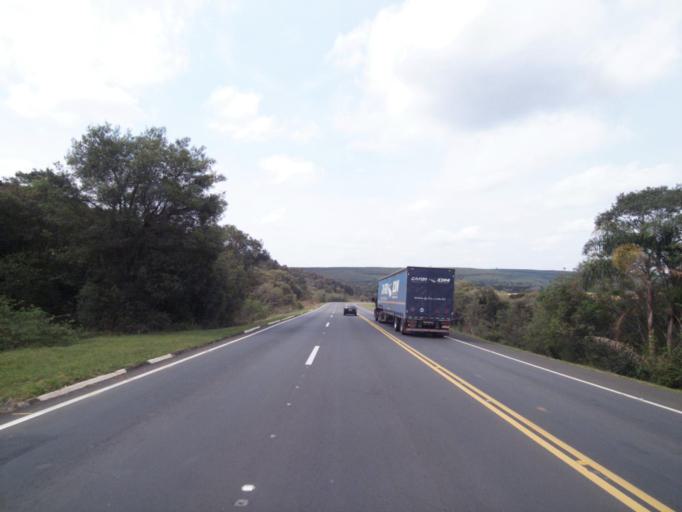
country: BR
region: Parana
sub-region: Irati
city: Irati
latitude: -25.4565
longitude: -50.4582
